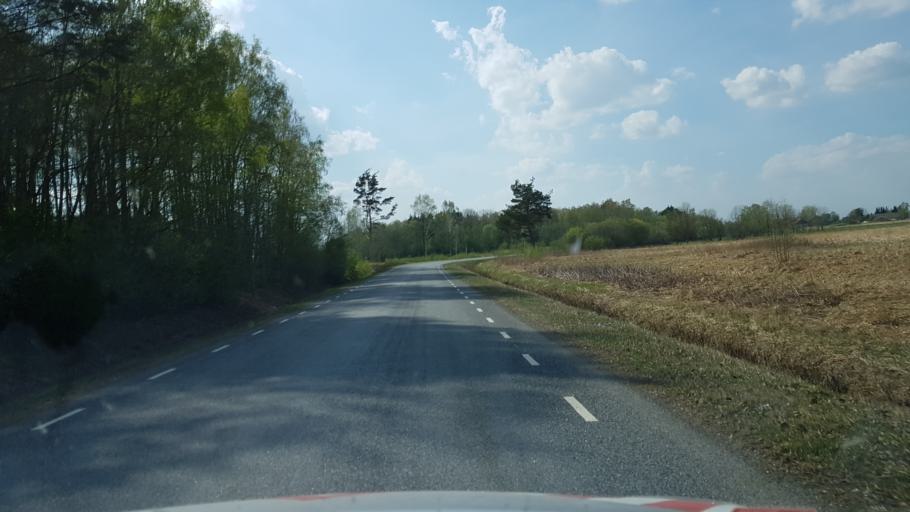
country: EE
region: Paernumaa
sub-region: Sauga vald
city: Sauga
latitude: 58.4397
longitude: 24.5623
